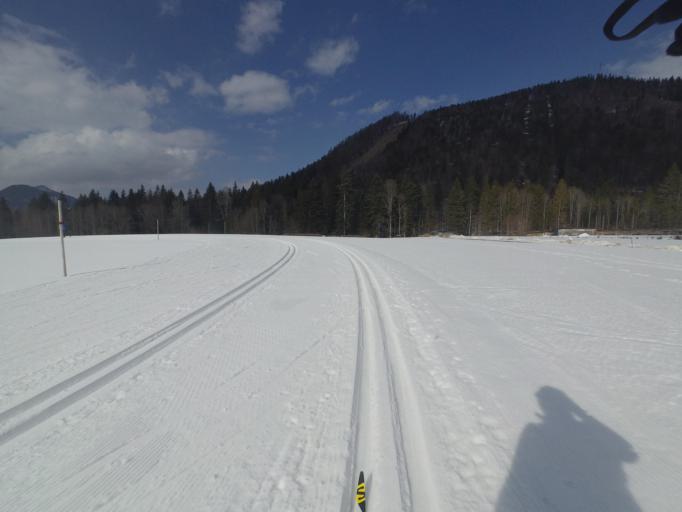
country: AT
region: Salzburg
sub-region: Politischer Bezirk Salzburg-Umgebung
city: Fuschl am See
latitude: 47.7660
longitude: 13.3212
